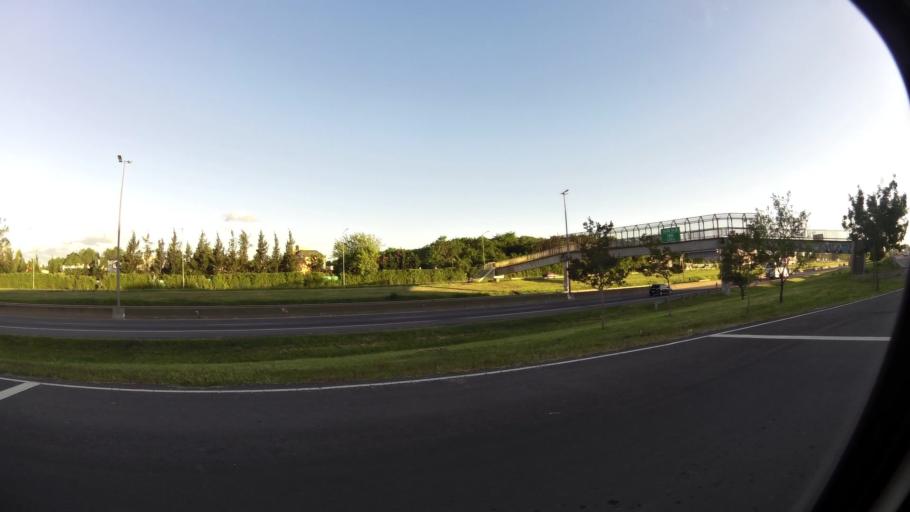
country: AR
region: Buenos Aires
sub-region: Partido de Quilmes
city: Quilmes
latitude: -34.7942
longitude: -58.1597
